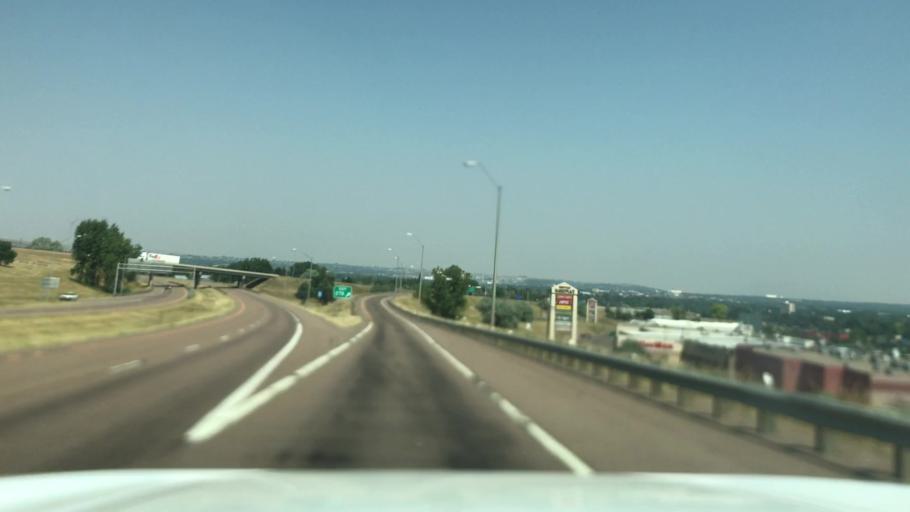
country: US
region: Montana
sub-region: Cascade County
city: Great Falls
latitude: 47.4820
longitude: -111.3469
